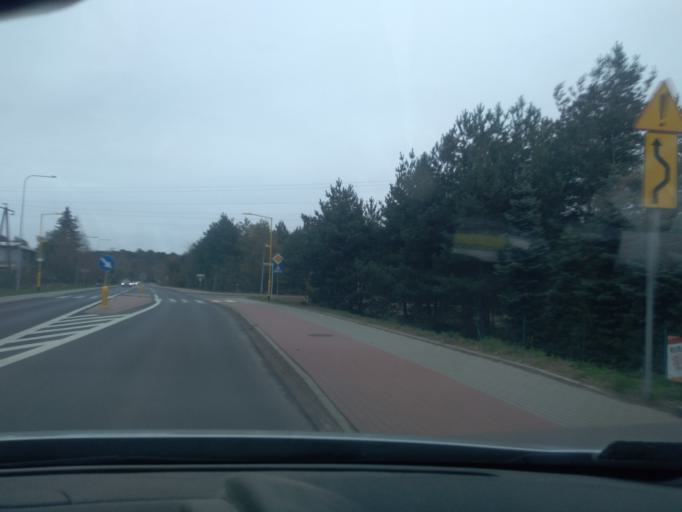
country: PL
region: Greater Poland Voivodeship
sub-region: Powiat poznanski
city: Murowana Goslina
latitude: 52.5439
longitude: 16.9726
